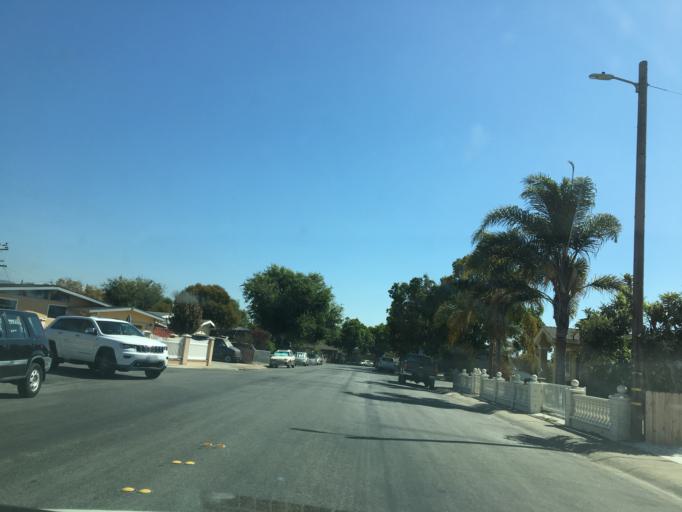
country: US
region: California
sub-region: Santa Clara County
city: East Foothills
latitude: 37.3893
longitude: -121.8348
